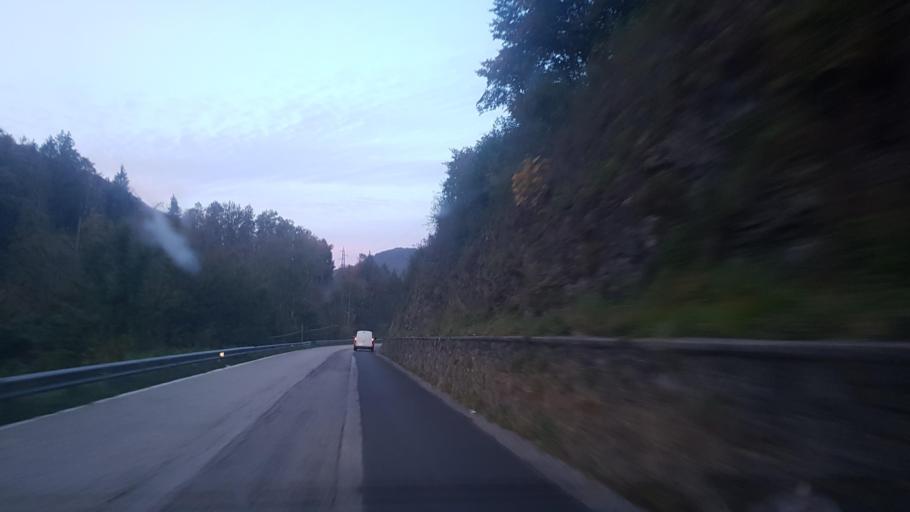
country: IT
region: Friuli Venezia Giulia
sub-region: Provincia di Udine
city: Chiaulis
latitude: 46.3870
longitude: 12.9985
